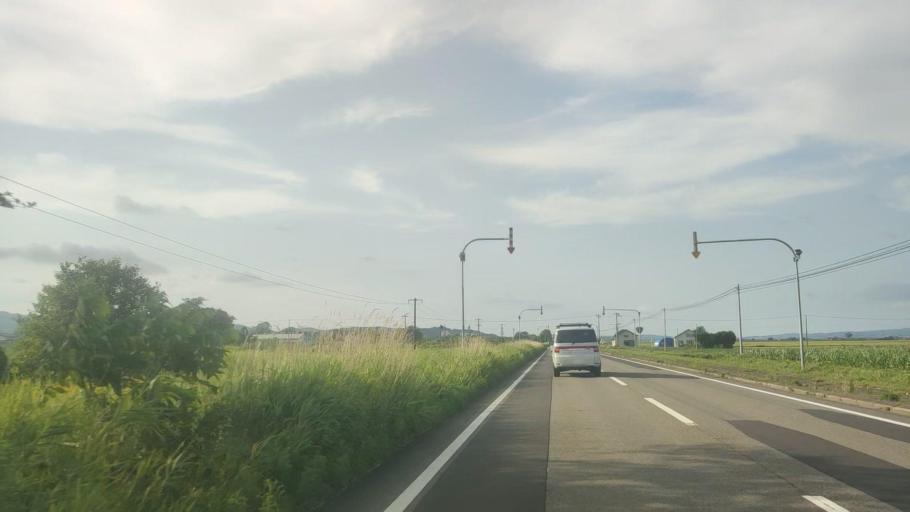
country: JP
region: Hokkaido
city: Chitose
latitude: 42.9606
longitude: 141.7977
